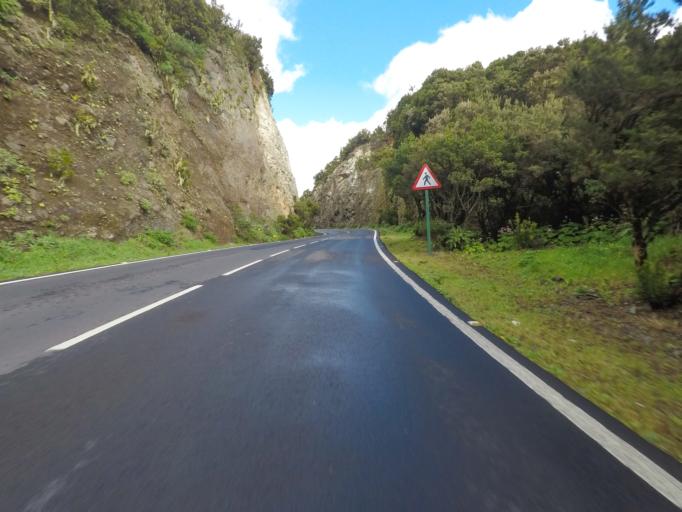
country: ES
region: Canary Islands
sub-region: Provincia de Santa Cruz de Tenerife
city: Alajero
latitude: 28.1104
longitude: -17.2173
